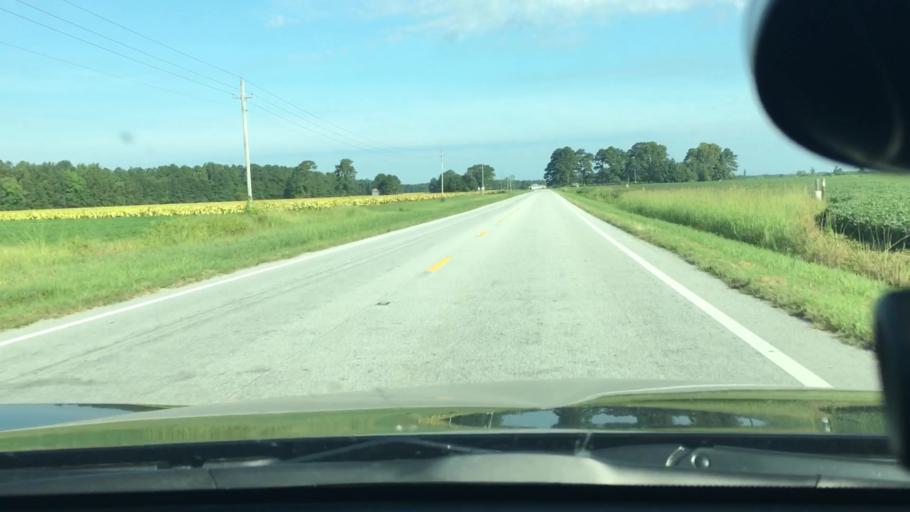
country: US
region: North Carolina
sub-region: Pitt County
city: Summerfield
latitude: 35.6643
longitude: -77.4760
